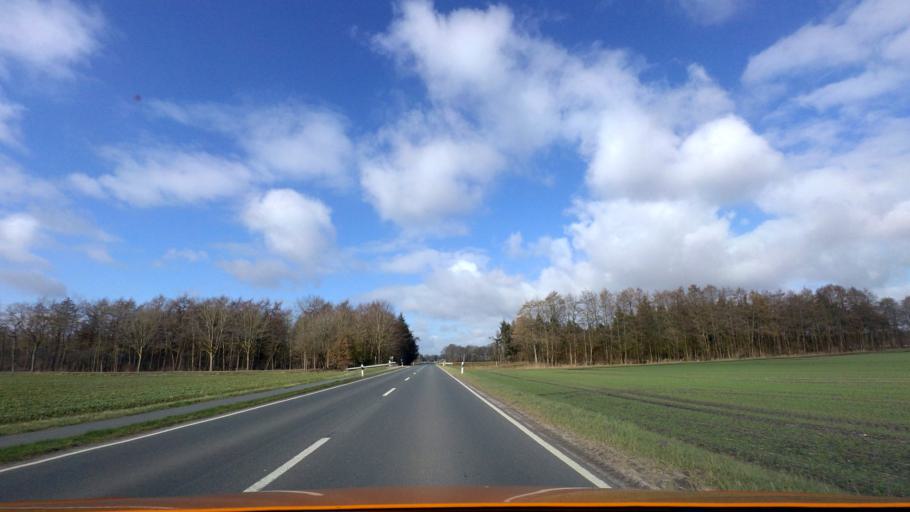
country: DE
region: Lower Saxony
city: Bosel
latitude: 53.0124
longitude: 7.9119
